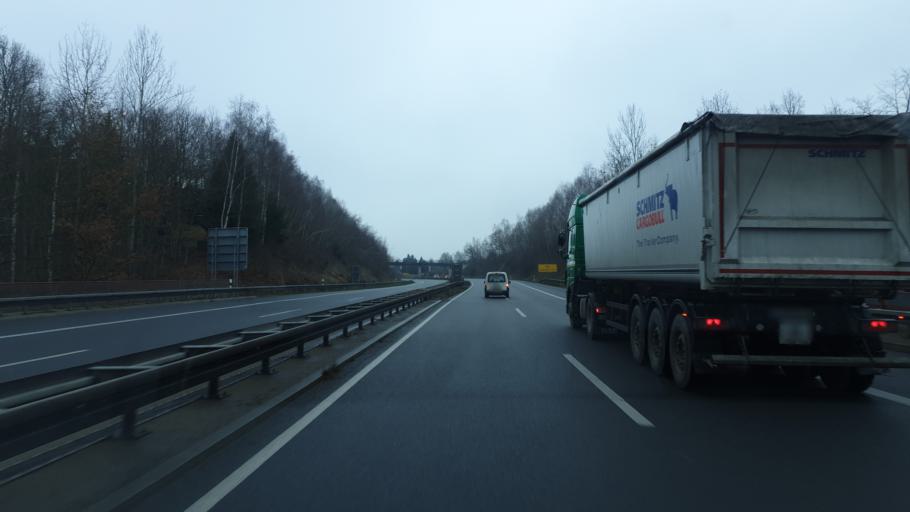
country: DE
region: Saxony
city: Zschopau
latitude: 50.7439
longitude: 13.0605
